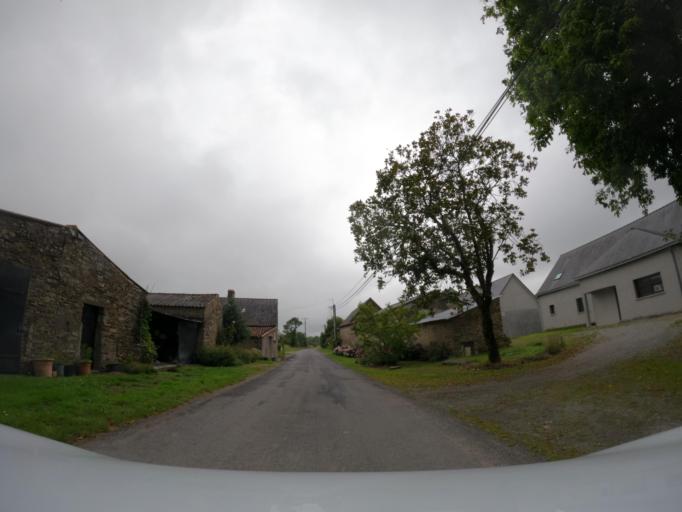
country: FR
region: Pays de la Loire
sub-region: Departement de la Loire-Atlantique
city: Saint-Mars-du-Desert
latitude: 47.3810
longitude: -1.4099
